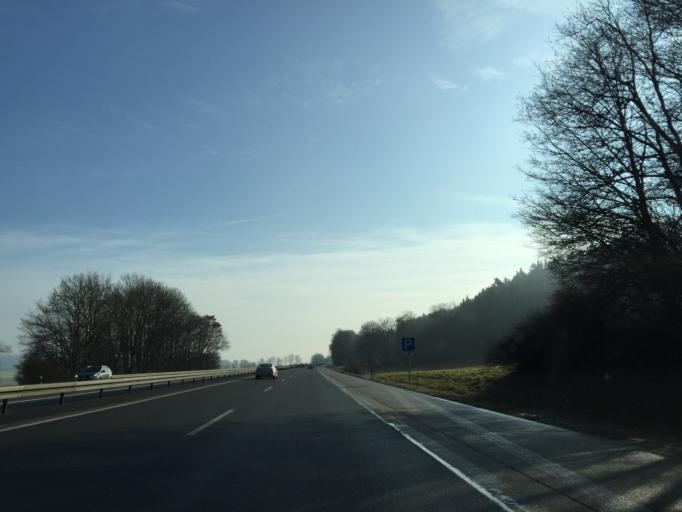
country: DE
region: Bavaria
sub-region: Regierungsbezirk Mittelfranken
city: Markt Taschendorf
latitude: 49.7631
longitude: 10.5375
